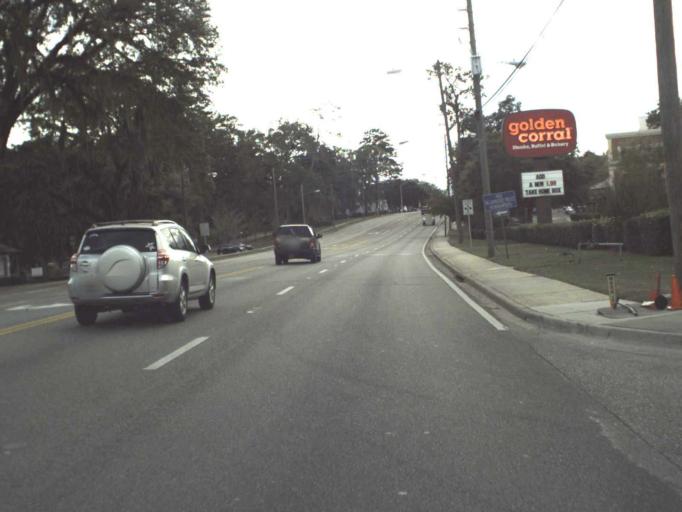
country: US
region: Florida
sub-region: Leon County
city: Tallahassee
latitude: 30.4614
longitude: -84.2815
